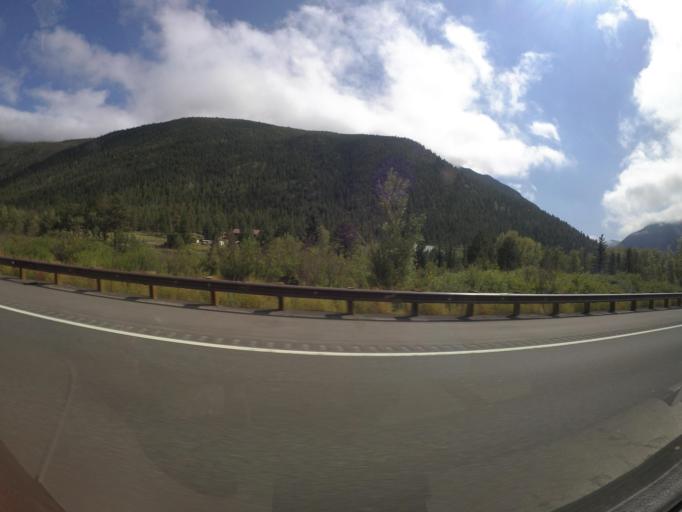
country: US
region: Colorado
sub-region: Clear Creek County
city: Georgetown
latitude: 39.7466
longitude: -105.6783
